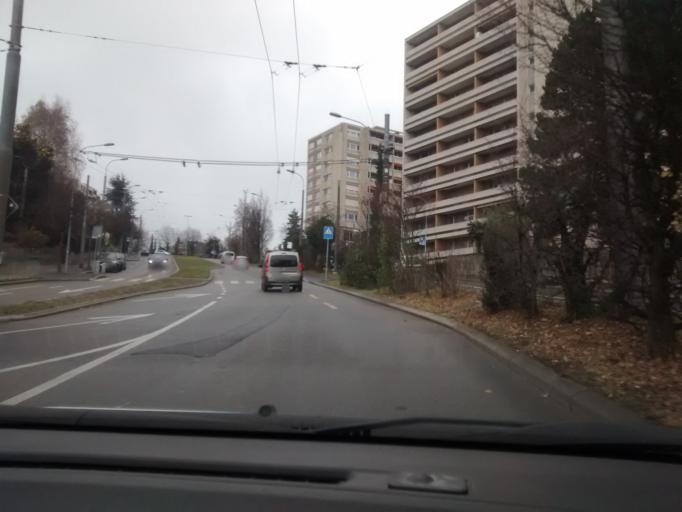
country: CH
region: Vaud
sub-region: Lausanne District
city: Blecherette
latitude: 46.5332
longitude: 6.6198
